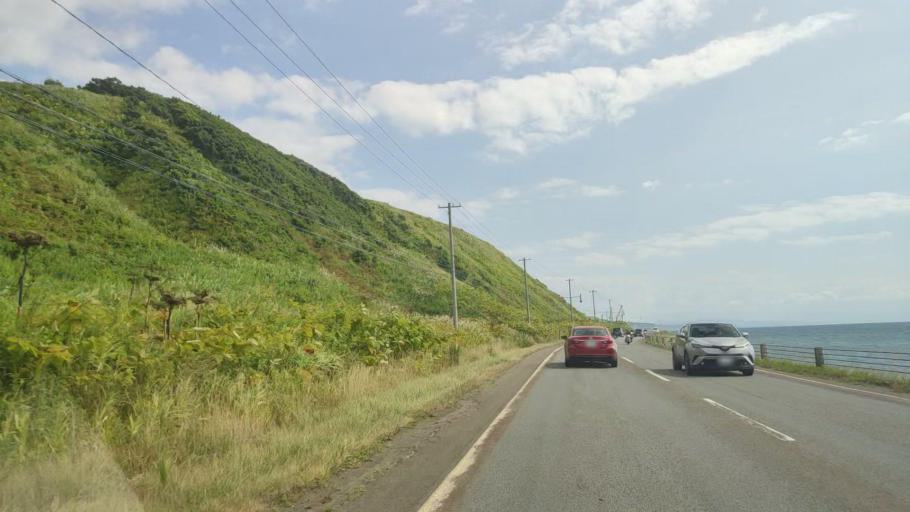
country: JP
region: Hokkaido
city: Rumoi
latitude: 44.0936
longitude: 141.6609
